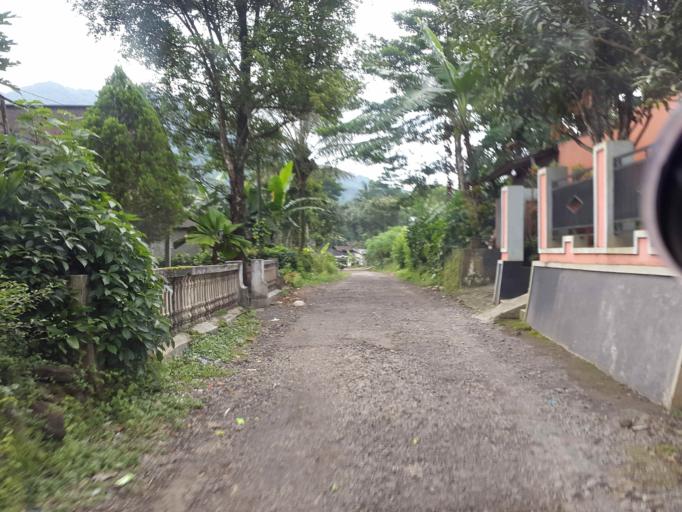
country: ID
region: Central Java
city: Randudongkal
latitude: -7.1873
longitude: 109.3336
